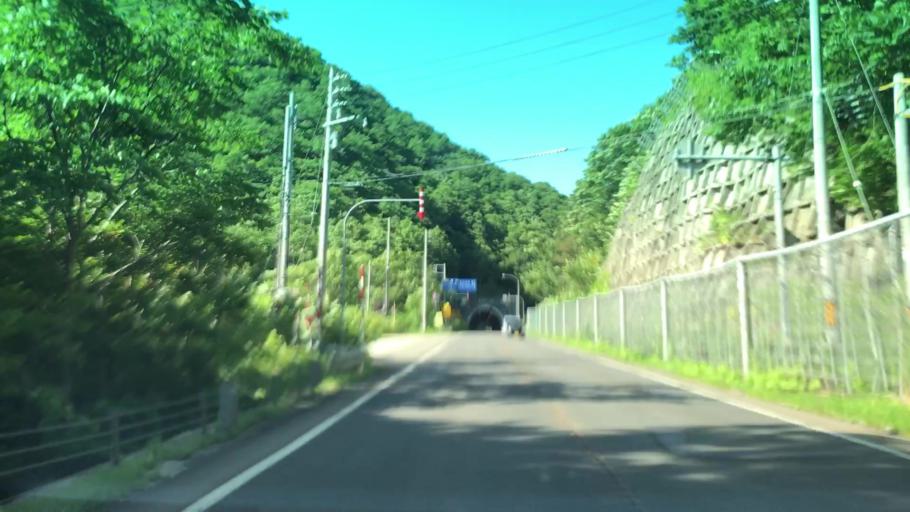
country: JP
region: Hokkaido
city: Iwanai
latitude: 43.0336
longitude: 140.6772
